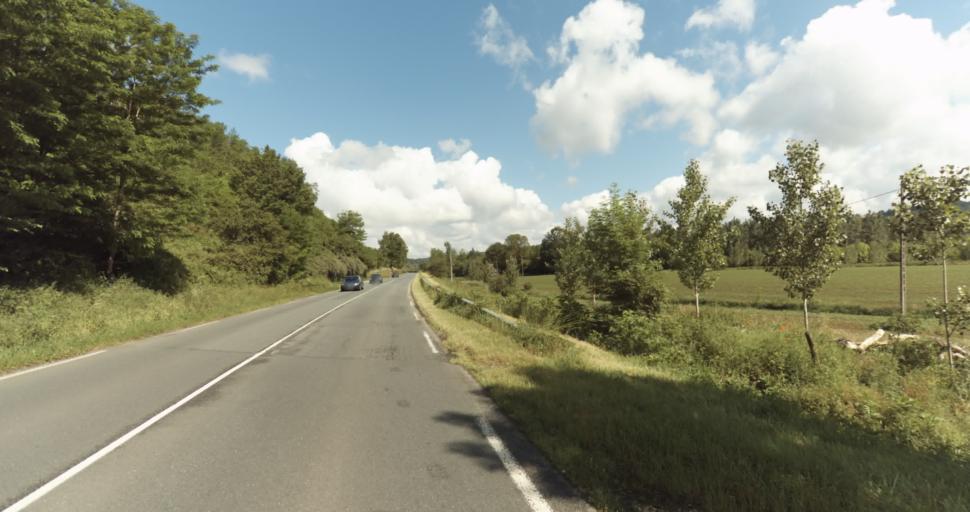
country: FR
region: Aquitaine
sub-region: Departement de la Dordogne
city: Le Bugue
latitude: 44.8376
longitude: 0.9351
